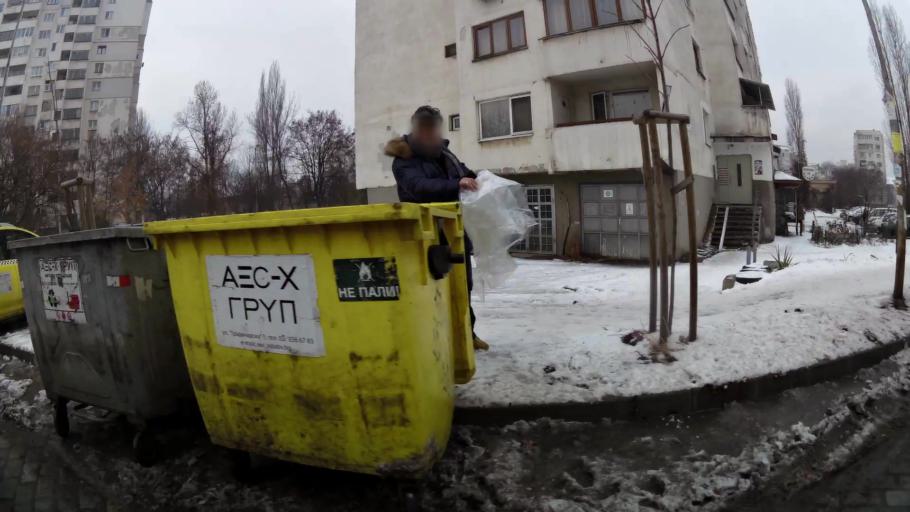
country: BG
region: Sofia-Capital
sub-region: Stolichna Obshtina
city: Sofia
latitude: 42.7095
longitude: 23.3017
